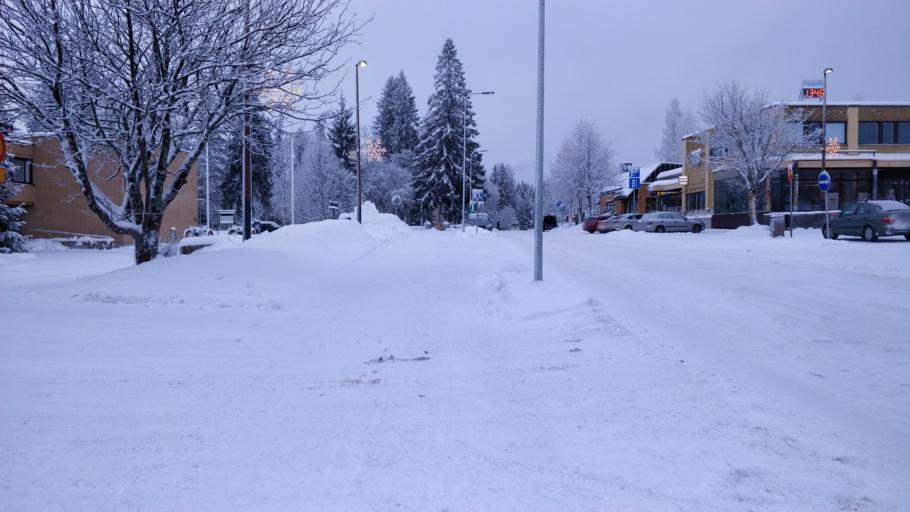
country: FI
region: Southern Savonia
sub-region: Mikkeli
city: Puumala
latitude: 61.5226
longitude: 28.1776
